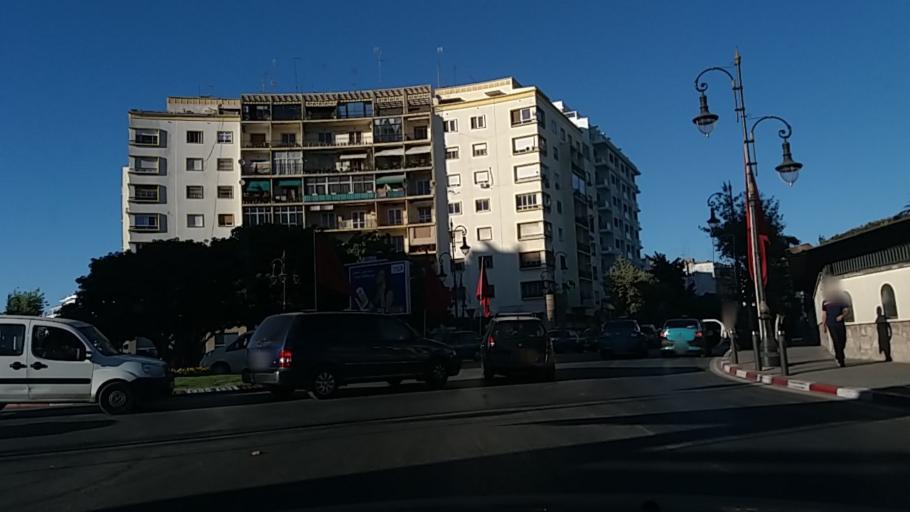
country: MA
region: Tanger-Tetouan
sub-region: Tanger-Assilah
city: Tangier
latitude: 35.7800
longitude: -5.8246
